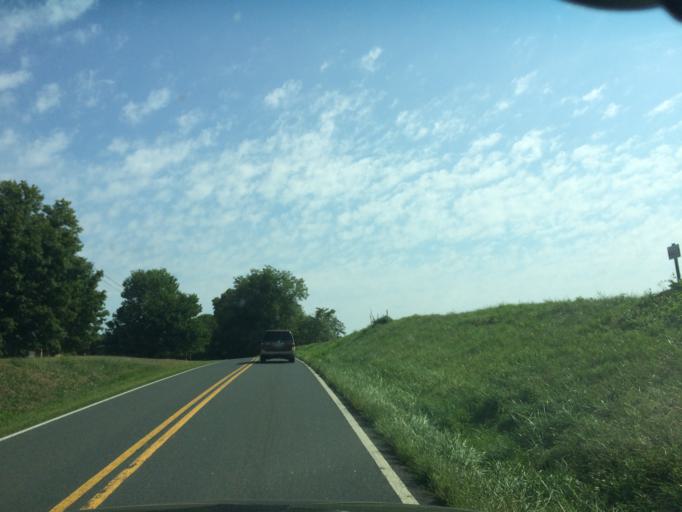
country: US
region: Maryland
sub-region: Carroll County
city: New Windsor
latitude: 39.5401
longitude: -77.0585
